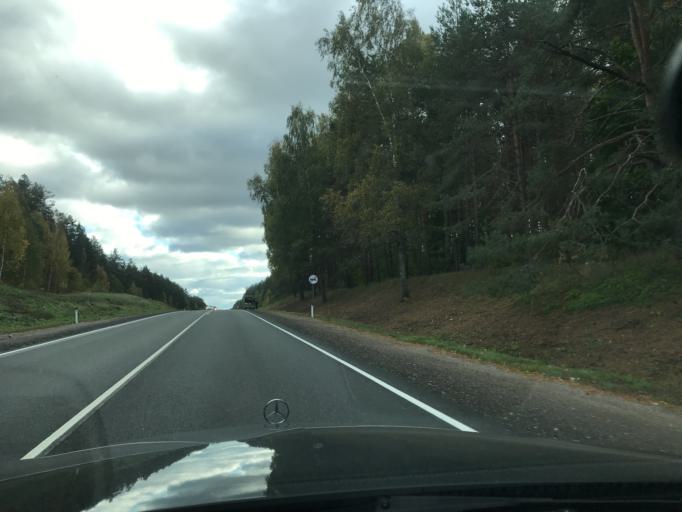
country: RU
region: Pskov
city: Opochka
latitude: 57.0021
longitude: 28.6153
